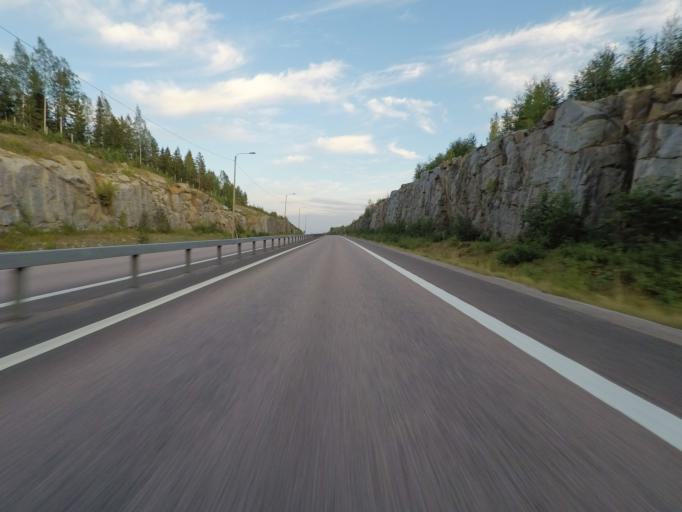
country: FI
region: Central Finland
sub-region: Jyvaeskylae
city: Toivakka
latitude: 62.0985
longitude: 25.9884
